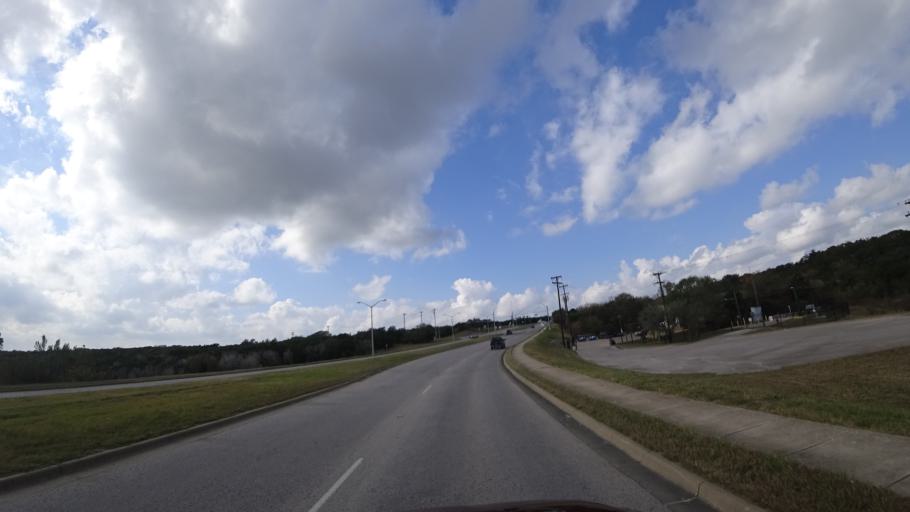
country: US
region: Texas
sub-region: Williamson County
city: Anderson Mill
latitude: 30.4601
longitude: -97.8387
